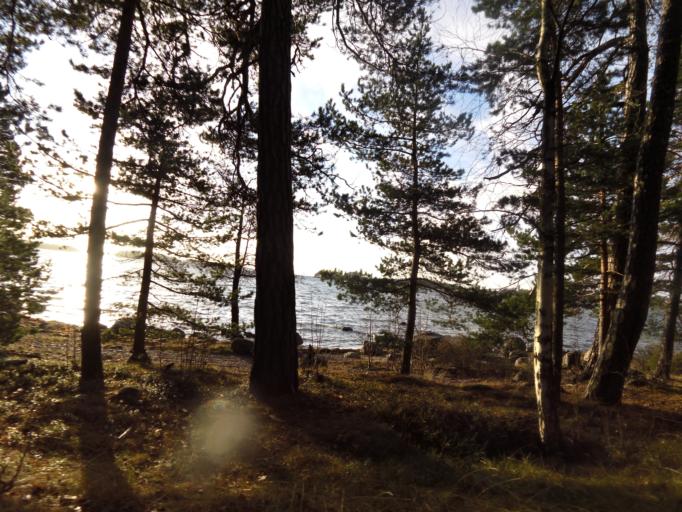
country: FI
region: Uusimaa
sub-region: Helsinki
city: Otaniemi
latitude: 60.1680
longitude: 24.8233
